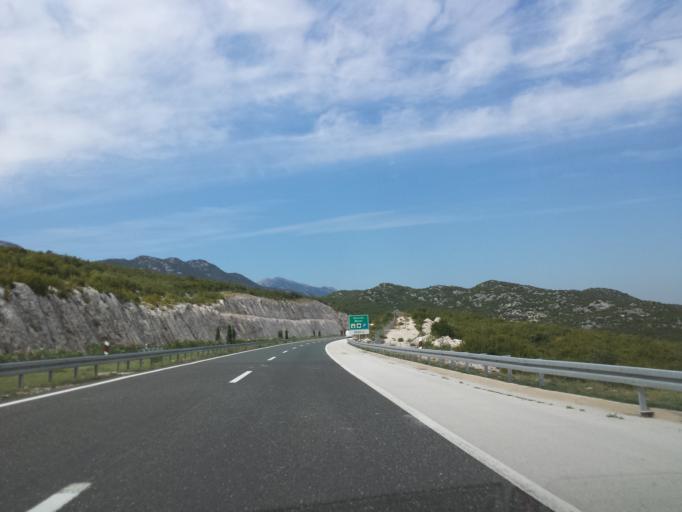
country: HR
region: Splitsko-Dalmatinska
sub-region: Grad Omis
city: Omis
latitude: 43.4791
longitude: 16.8129
